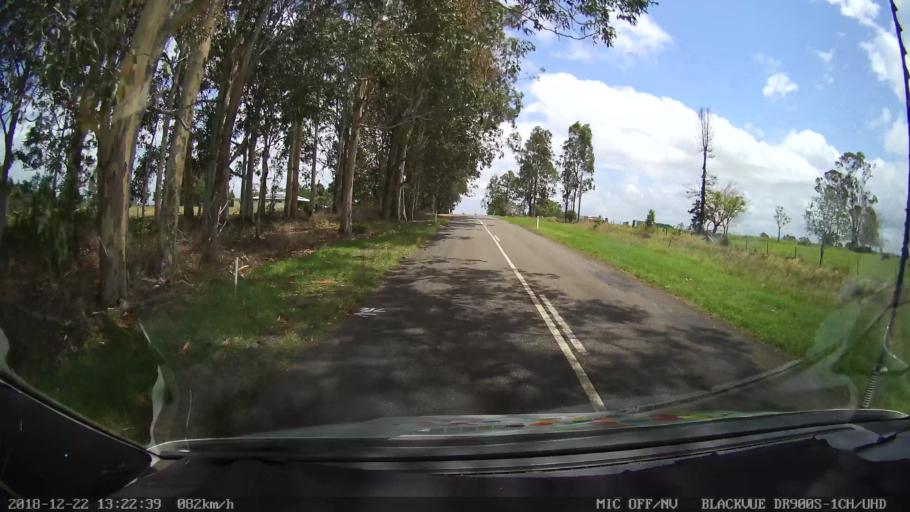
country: AU
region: New South Wales
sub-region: Clarence Valley
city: Coutts Crossing
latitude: -29.7892
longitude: 152.9106
